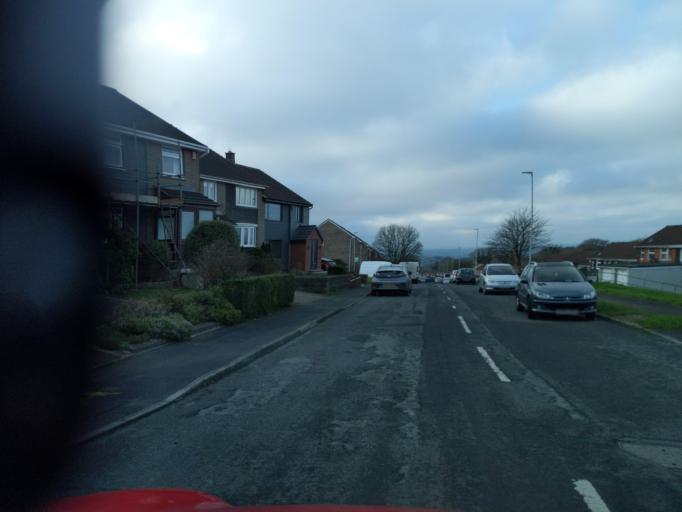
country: GB
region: England
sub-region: Devon
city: Yelverton
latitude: 50.4363
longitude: -4.1126
